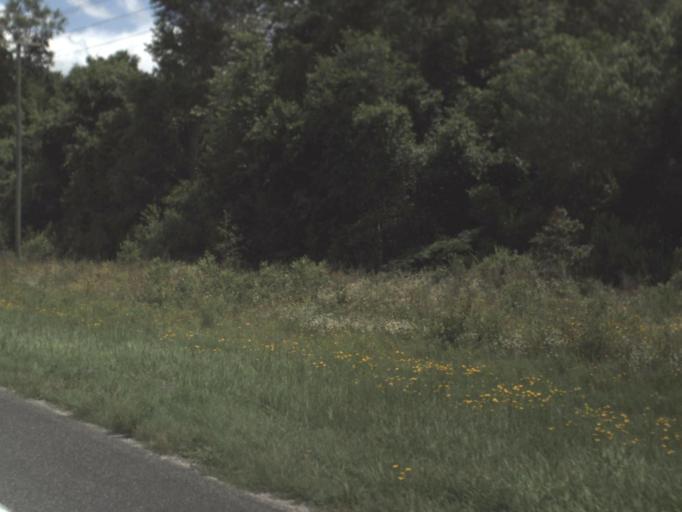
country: US
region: Florida
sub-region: Alachua County
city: High Springs
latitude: 29.8986
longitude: -82.6843
